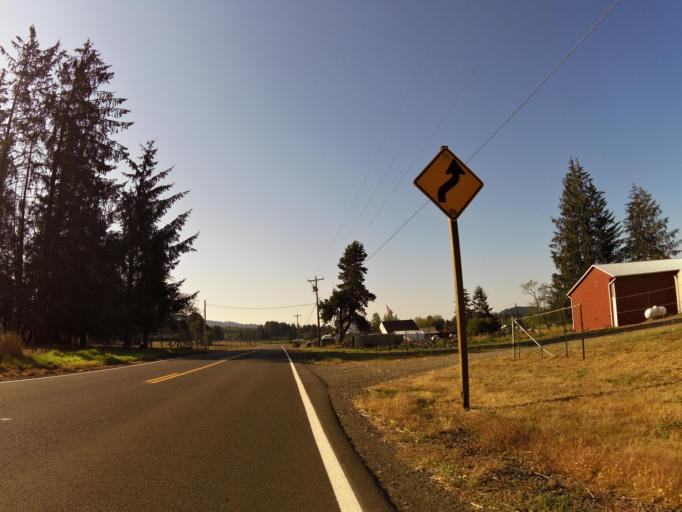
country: US
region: Oregon
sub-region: Tillamook County
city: Tillamook
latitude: 45.3947
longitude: -123.7933
